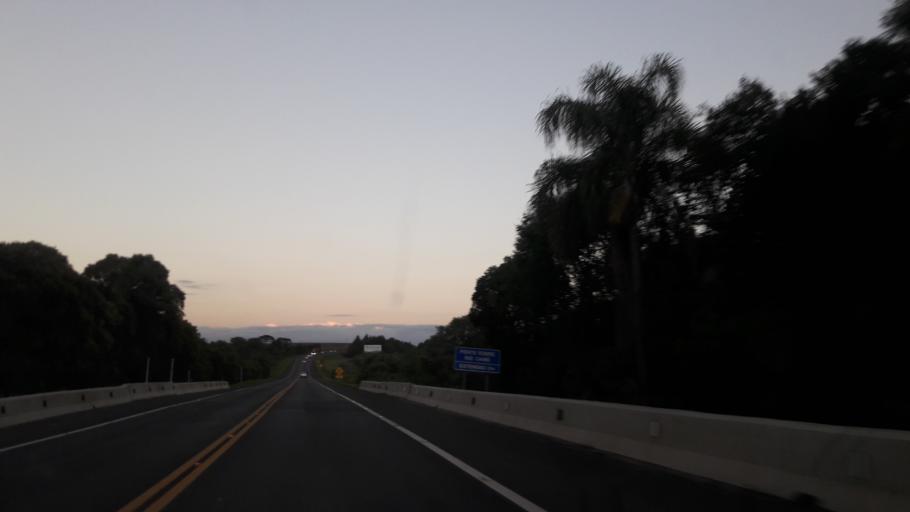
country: BR
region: Parana
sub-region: Palmeira
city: Palmeira
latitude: -25.4232
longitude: -50.0951
